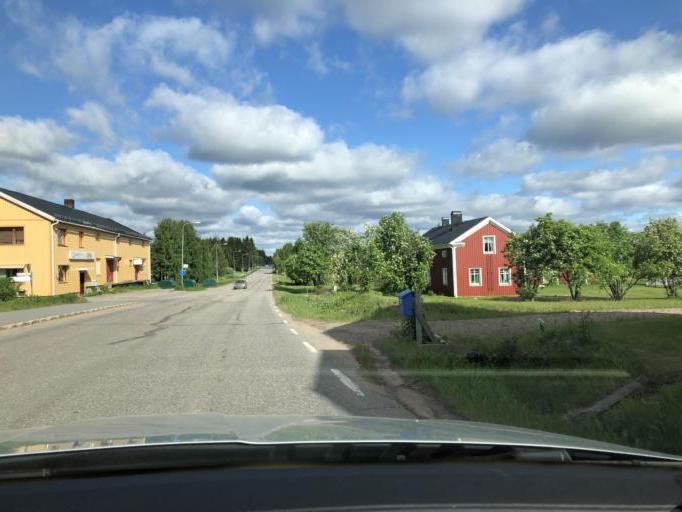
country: SE
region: Norrbotten
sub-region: Pajala Kommun
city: Pajala
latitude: 67.2176
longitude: 23.3576
